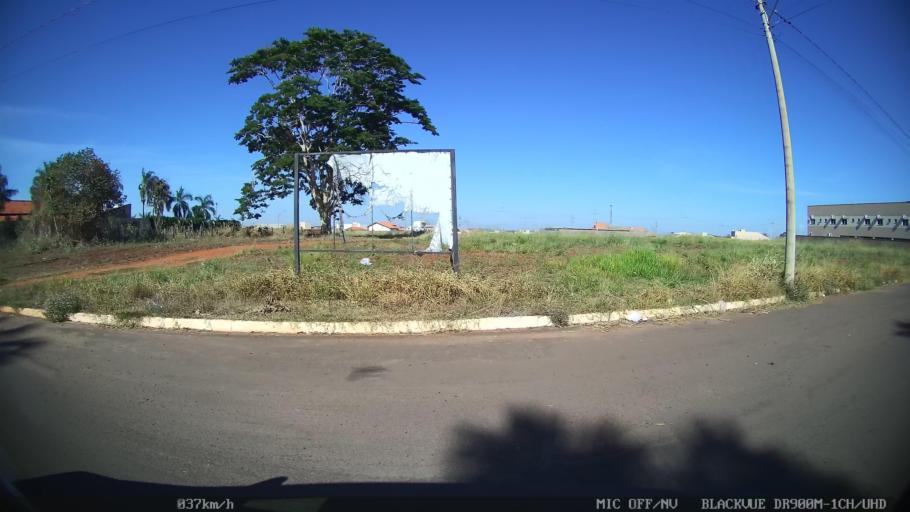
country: BR
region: Sao Paulo
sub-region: Olimpia
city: Olimpia
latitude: -20.7559
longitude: -48.9128
